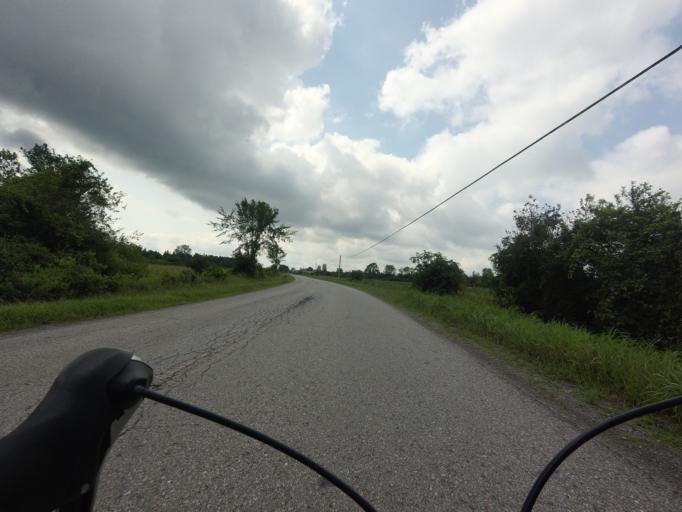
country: CA
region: Ontario
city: Brockville
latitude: 44.7931
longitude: -75.7206
